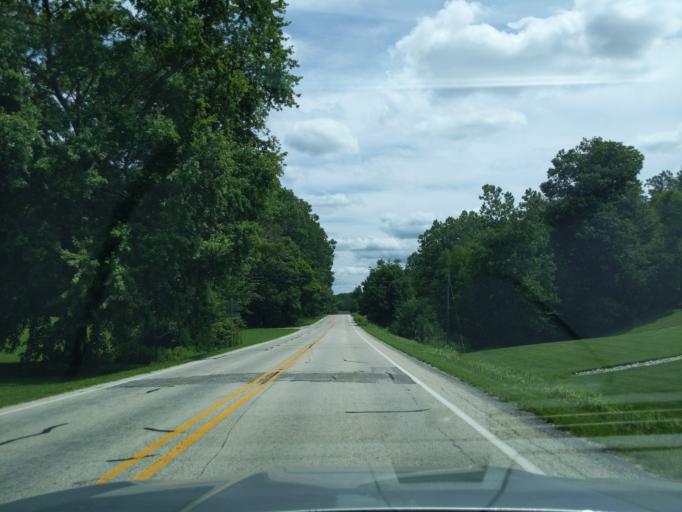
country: US
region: Indiana
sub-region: Ripley County
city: Batesville
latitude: 39.3085
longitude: -85.2456
